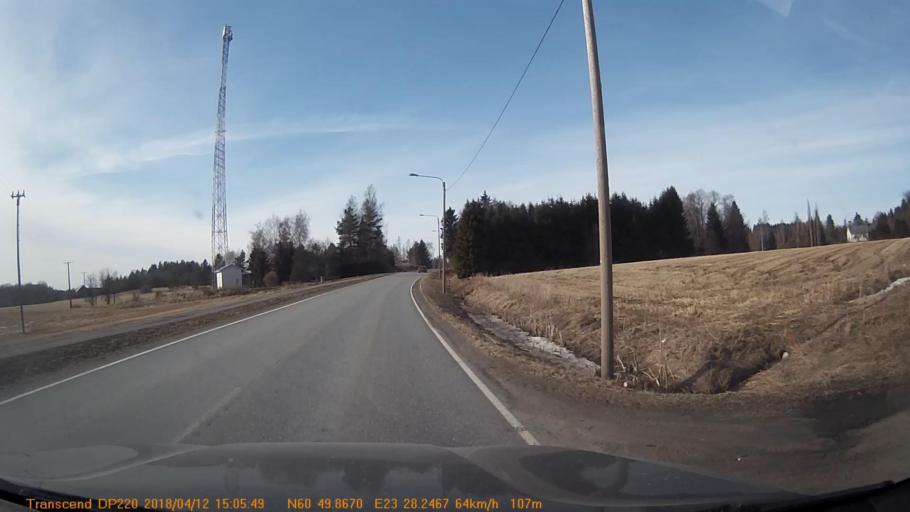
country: FI
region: Haeme
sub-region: Forssa
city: Jokioinen
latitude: 60.8313
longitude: 23.4704
